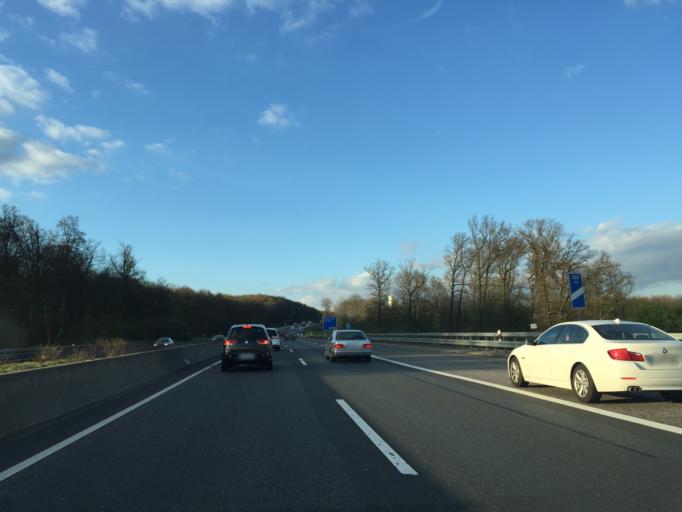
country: DE
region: Hesse
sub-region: Regierungsbezirk Giessen
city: Reiskirchen
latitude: 50.5952
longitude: 8.8135
